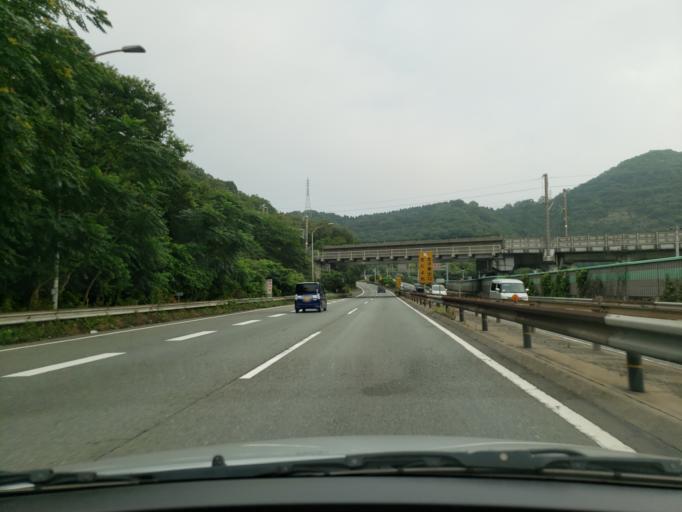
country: JP
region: Hyogo
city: Himeji
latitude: 34.8303
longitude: 134.6324
